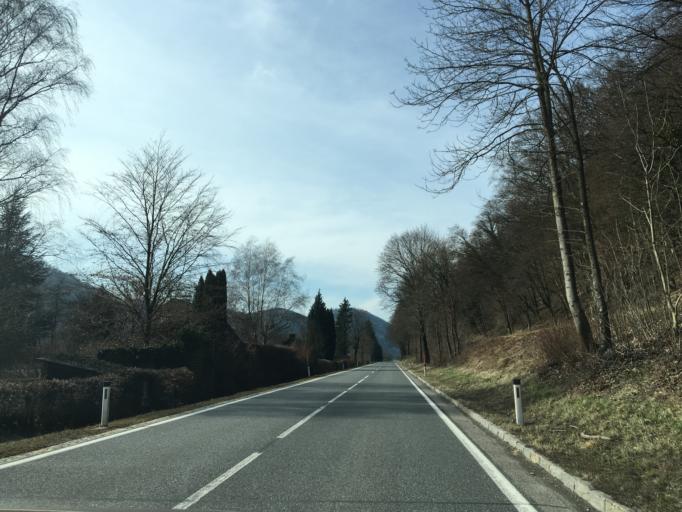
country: AT
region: Lower Austria
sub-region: Politischer Bezirk Melk
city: Nochling
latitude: 48.1971
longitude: 14.9962
